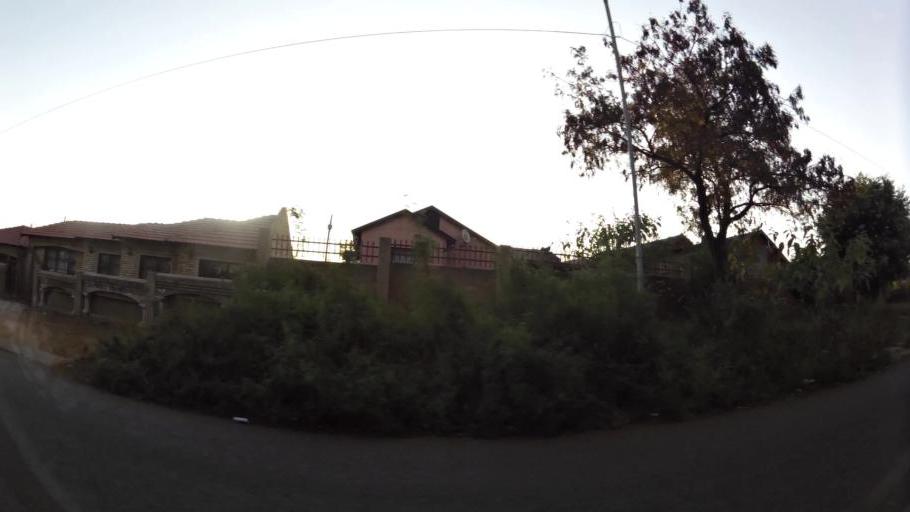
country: ZA
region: Gauteng
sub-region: City of Tshwane Metropolitan Municipality
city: Pretoria
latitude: -25.7405
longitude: 28.1411
